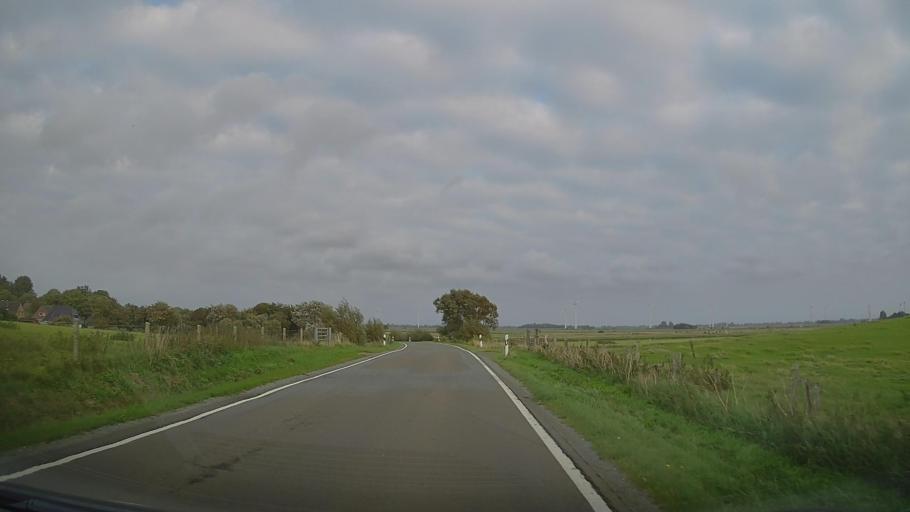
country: DE
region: Schleswig-Holstein
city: Uelvesbull
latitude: 54.4151
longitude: 8.9168
